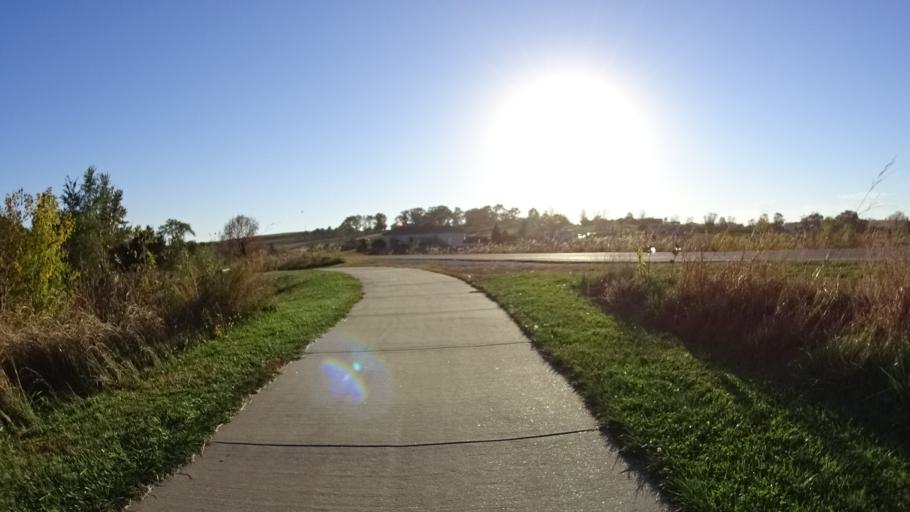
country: US
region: Nebraska
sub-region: Sarpy County
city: Papillion
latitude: 41.1357
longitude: -96.0734
